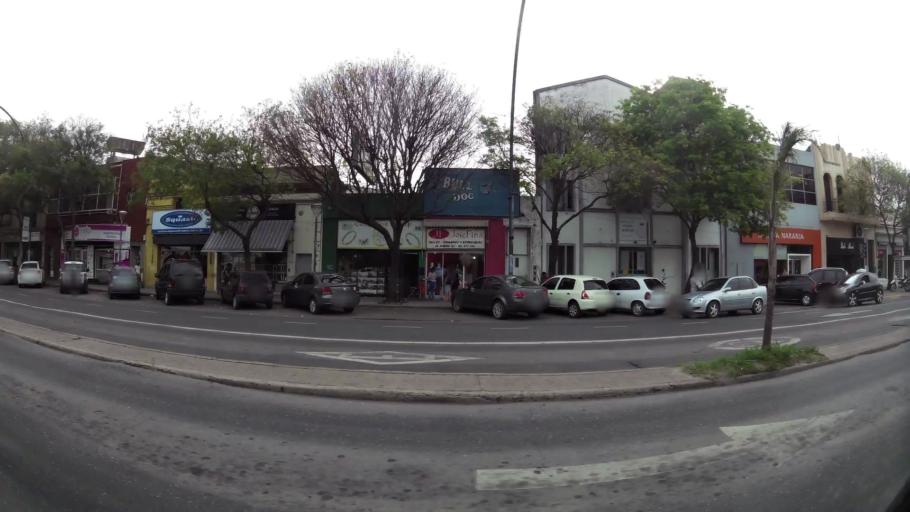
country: AR
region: Santa Fe
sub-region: Departamento de Rosario
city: Rosario
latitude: -32.9185
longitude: -60.6830
